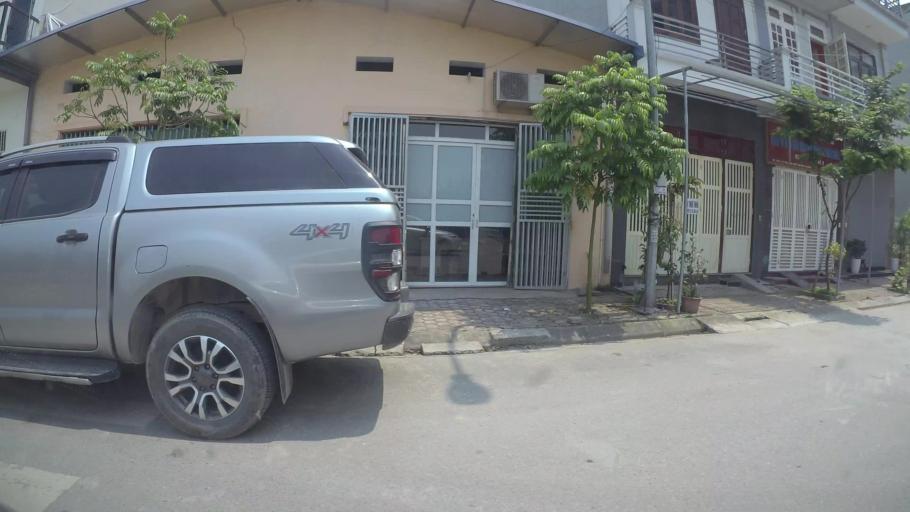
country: VN
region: Ha Noi
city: Ha Dong
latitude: 20.9852
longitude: 105.7722
